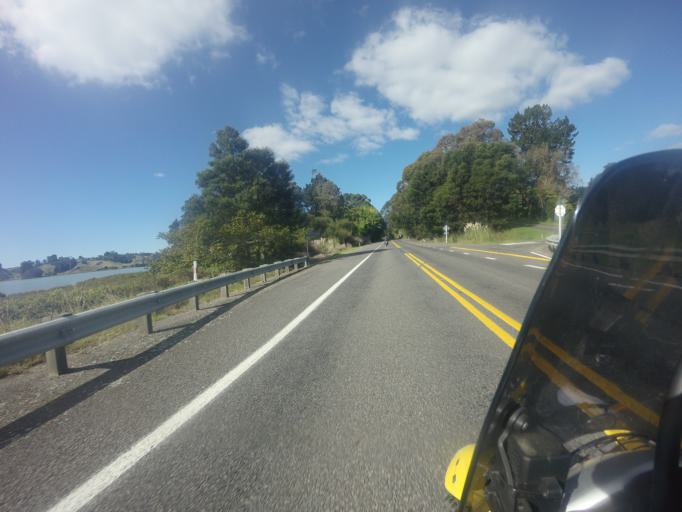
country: NZ
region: Bay of Plenty
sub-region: Opotiki District
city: Opotiki
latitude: -38.0441
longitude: 177.1499
